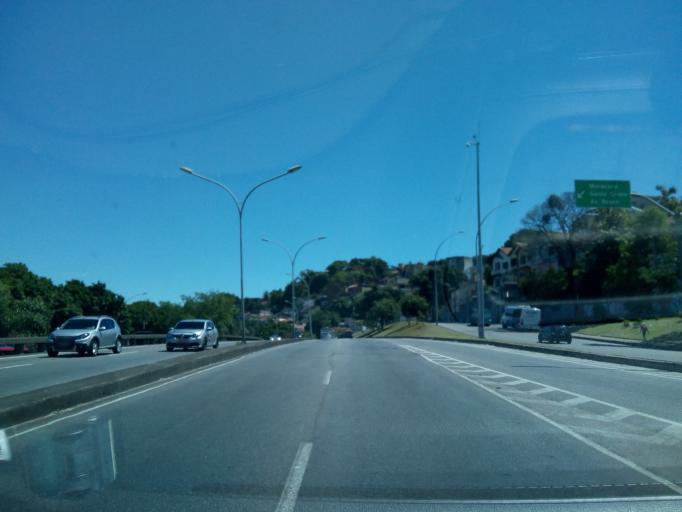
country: BR
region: Rio de Janeiro
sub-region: Rio De Janeiro
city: Rio de Janeiro
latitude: -22.9176
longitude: -43.1944
